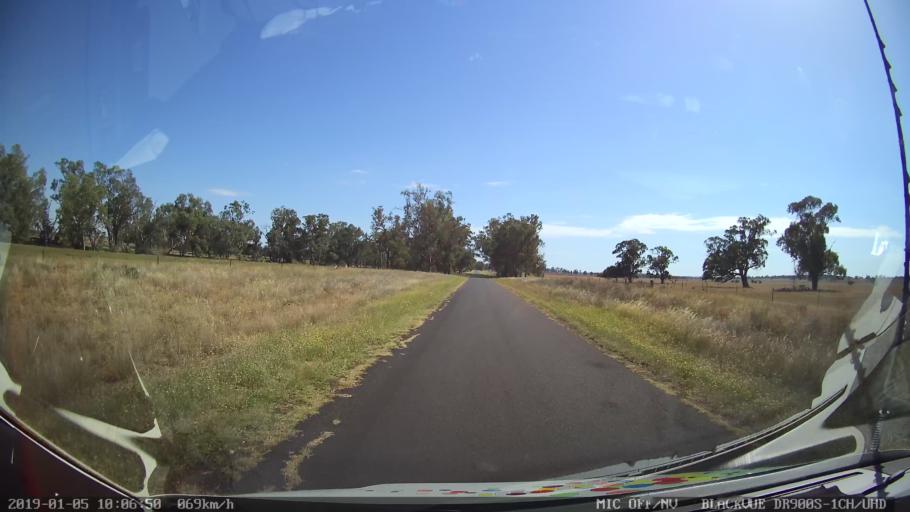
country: AU
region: New South Wales
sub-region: Gilgandra
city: Gilgandra
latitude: -31.6544
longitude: 148.8711
